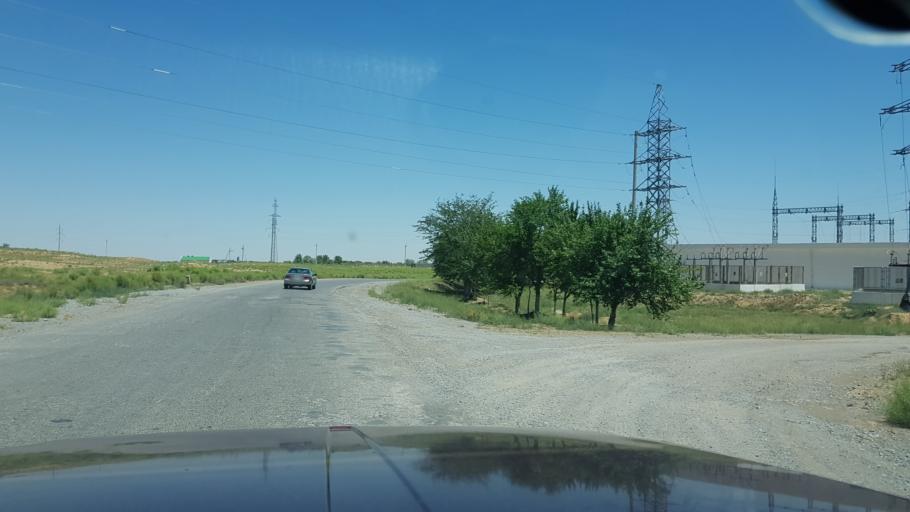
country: TM
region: Ahal
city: Annau
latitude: 37.8836
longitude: 58.7308
